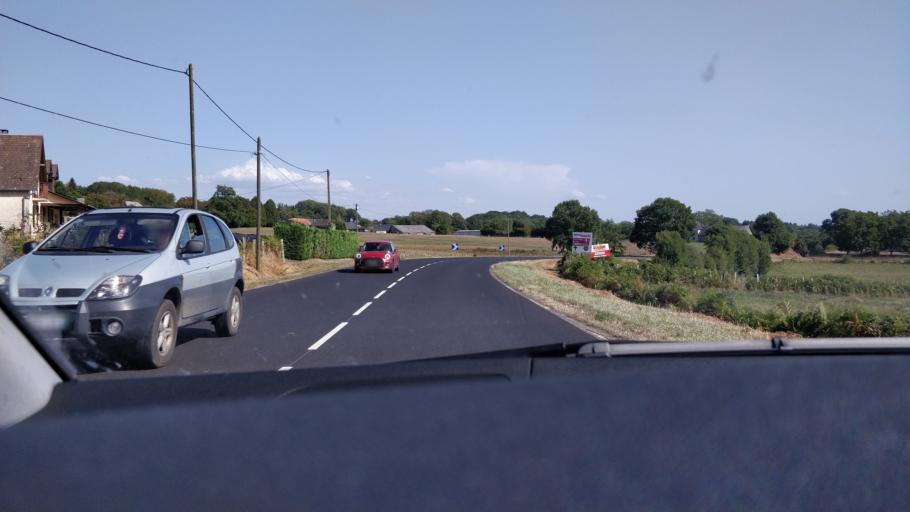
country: FR
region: Limousin
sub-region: Departement de la Correze
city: Uzerche
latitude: 45.4743
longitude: 1.5384
